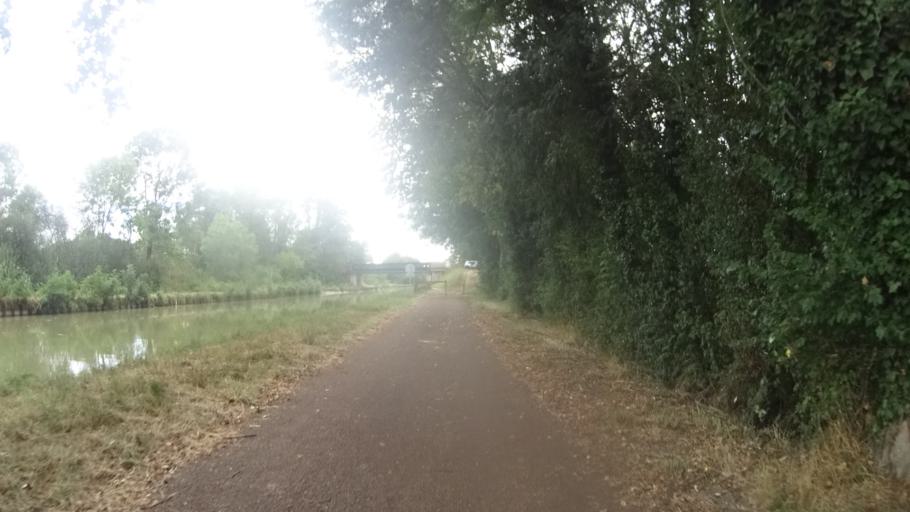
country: FR
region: Bourgogne
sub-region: Departement de la Nievre
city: Sermoise-sur-Loire
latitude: 46.9614
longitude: 3.1841
